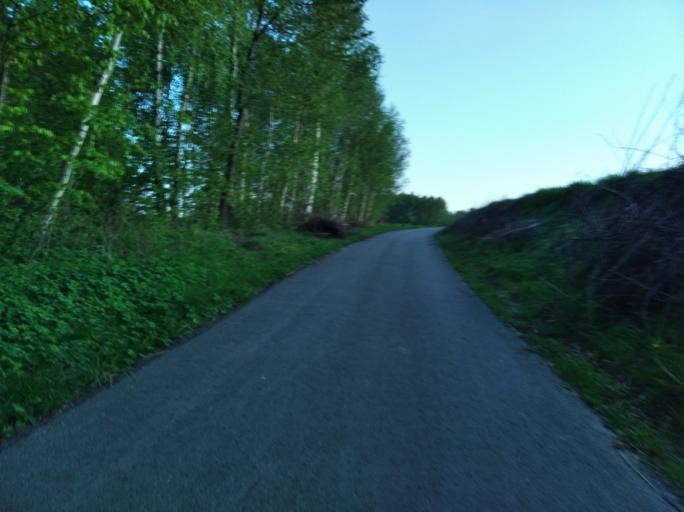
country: PL
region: Subcarpathian Voivodeship
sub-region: Powiat strzyzowski
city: Czudec
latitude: 49.9175
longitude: 21.8074
